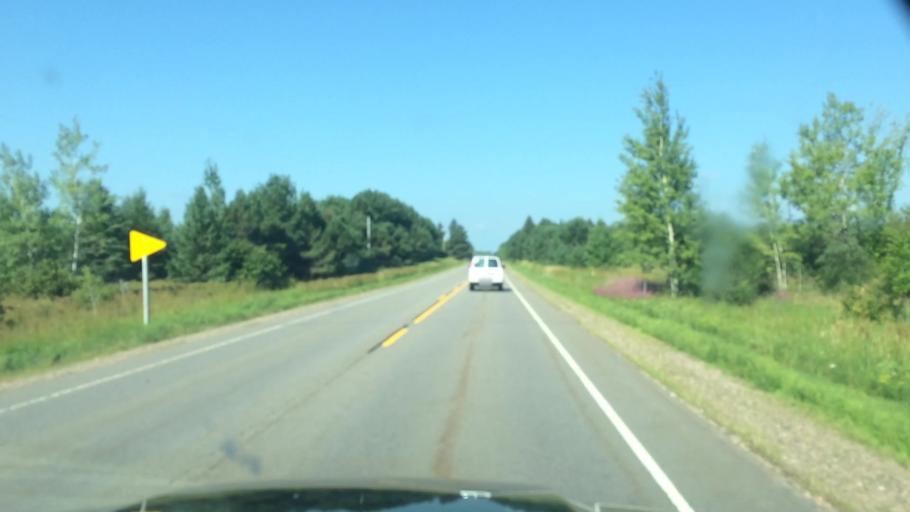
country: US
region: Wisconsin
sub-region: Lincoln County
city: Merrill
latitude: 45.1484
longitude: -89.4407
